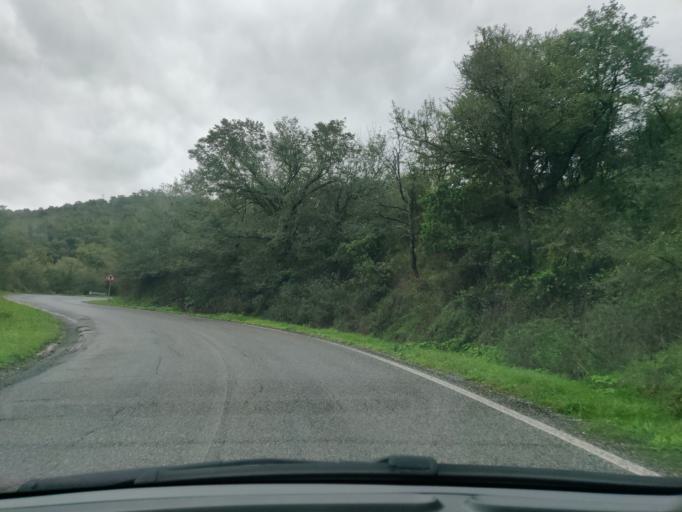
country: IT
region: Latium
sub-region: Citta metropolitana di Roma Capitale
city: Allumiere
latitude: 42.1443
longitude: 11.8848
